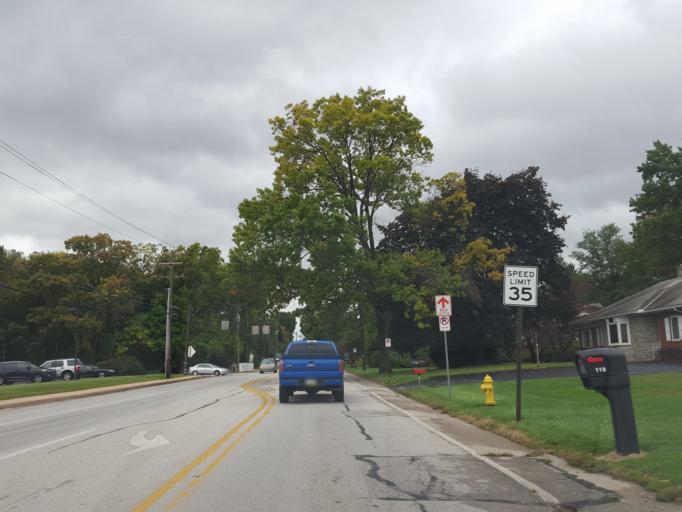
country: US
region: Pennsylvania
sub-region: York County
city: East York
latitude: 39.9721
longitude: -76.6797
